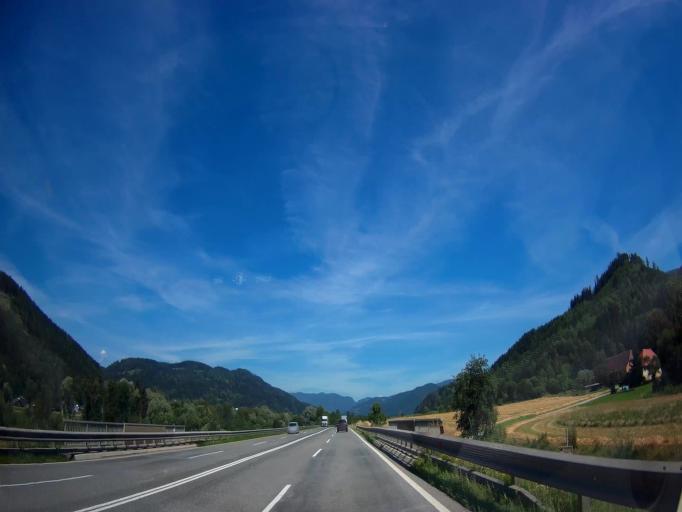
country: AT
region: Carinthia
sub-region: Politischer Bezirk Sankt Veit an der Glan
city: Micheldorf
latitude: 46.9055
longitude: 14.4386
